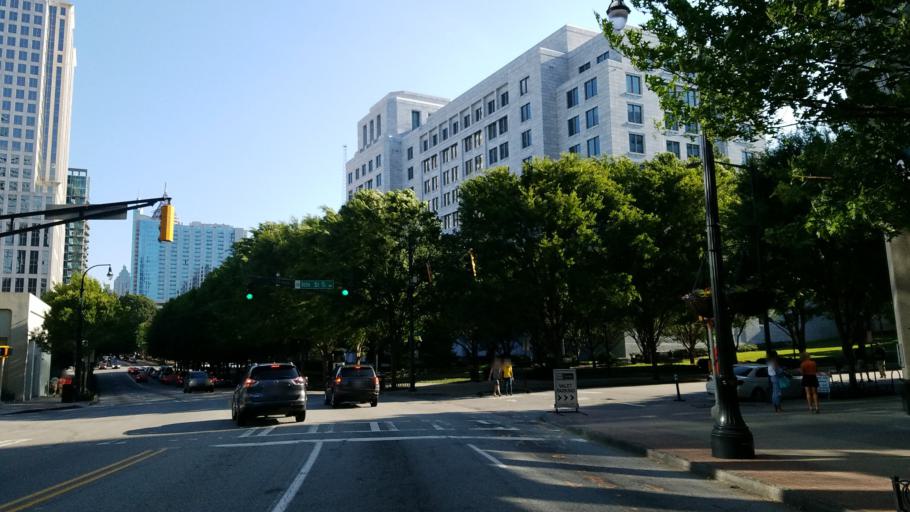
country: US
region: Georgia
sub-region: Fulton County
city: Atlanta
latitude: 33.7835
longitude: -84.3836
